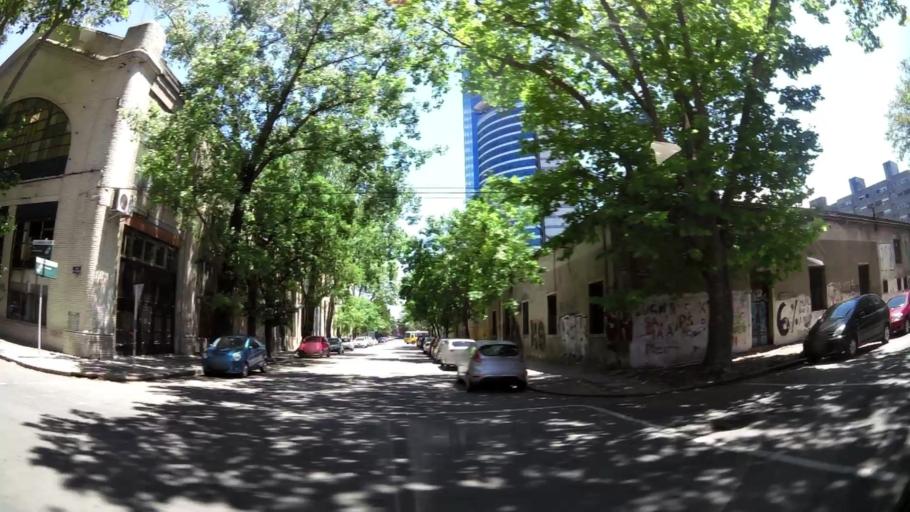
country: UY
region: Montevideo
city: Montevideo
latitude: -34.8921
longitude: -56.1929
